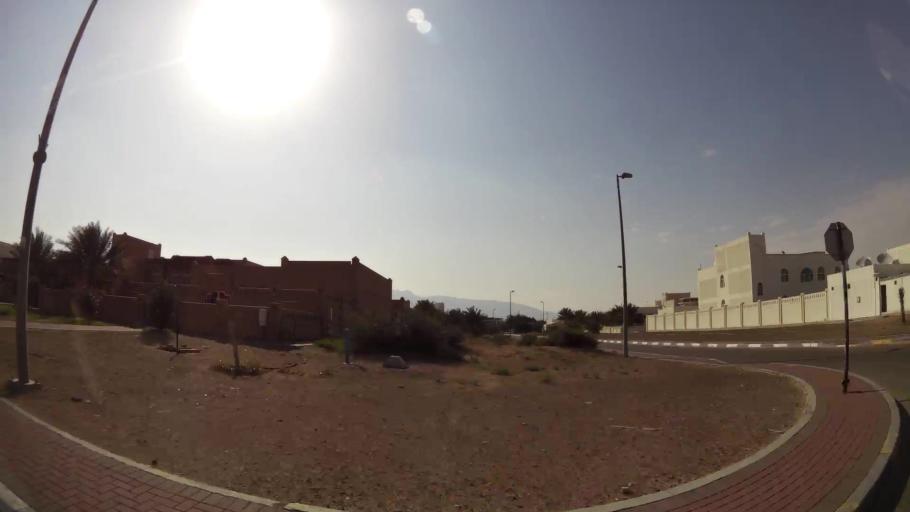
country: AE
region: Abu Dhabi
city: Al Ain
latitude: 24.0724
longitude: 55.8731
